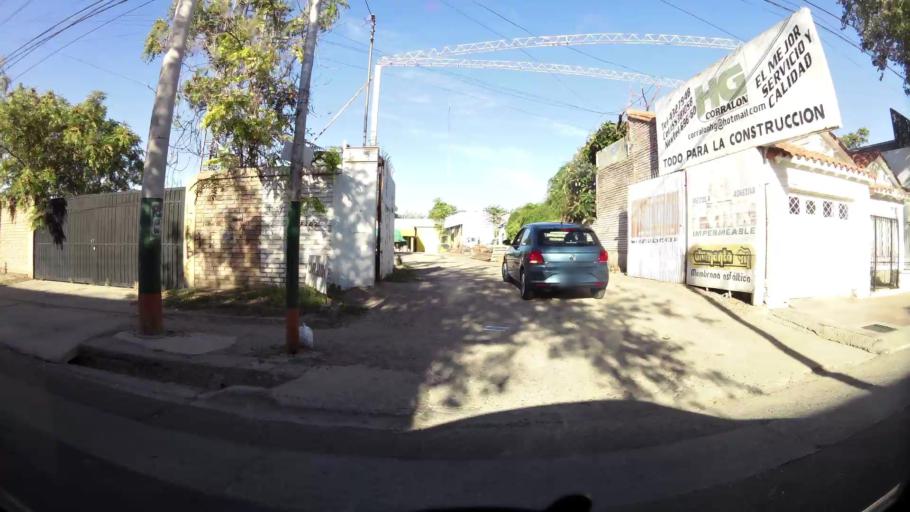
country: AR
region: Mendoza
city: Mendoza
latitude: -32.9050
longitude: -68.8288
